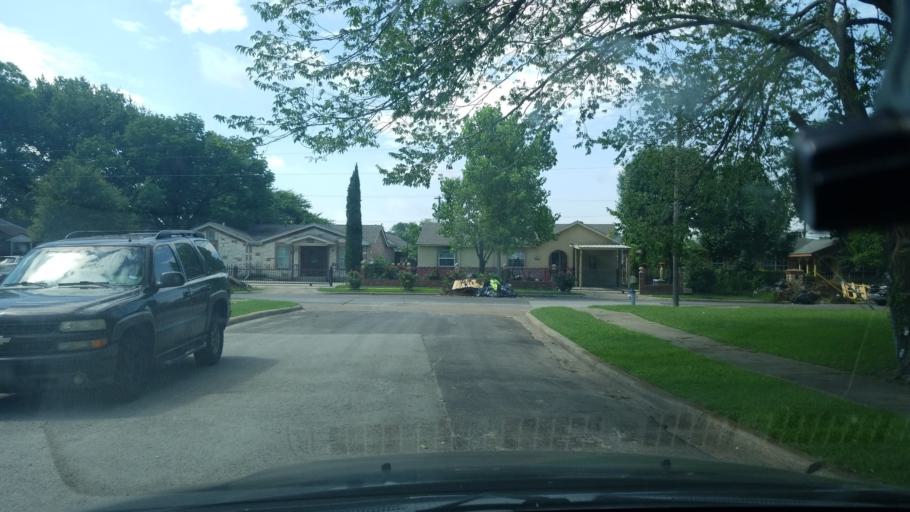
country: US
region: Texas
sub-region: Dallas County
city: Balch Springs
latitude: 32.7357
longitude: -96.6867
